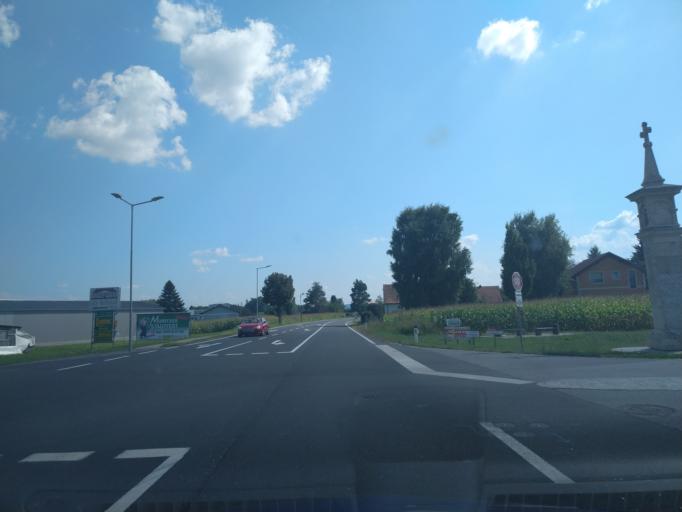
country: AT
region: Styria
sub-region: Politischer Bezirk Leibnitz
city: Gabersdorf
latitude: 46.7844
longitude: 15.5645
